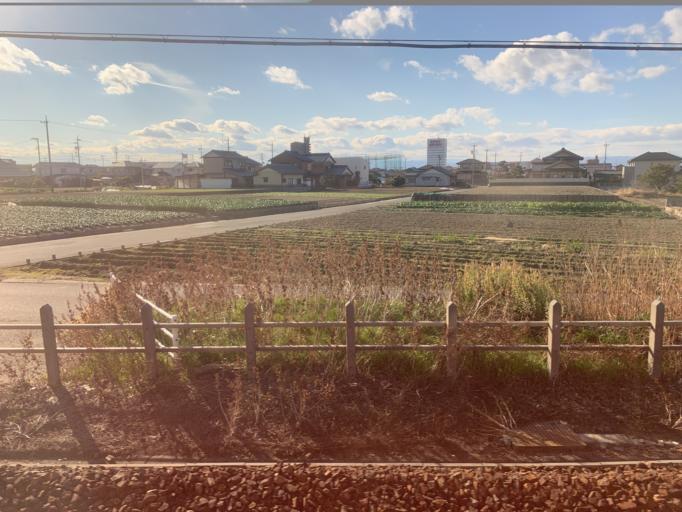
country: JP
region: Aichi
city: Inazawa
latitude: 35.2374
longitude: 136.8284
